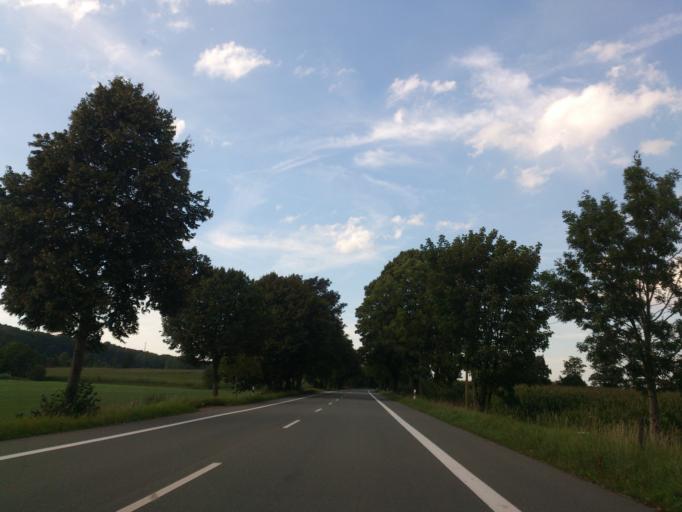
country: DE
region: North Rhine-Westphalia
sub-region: Regierungsbezirk Detmold
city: Willebadessen
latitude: 51.5908
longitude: 9.0356
